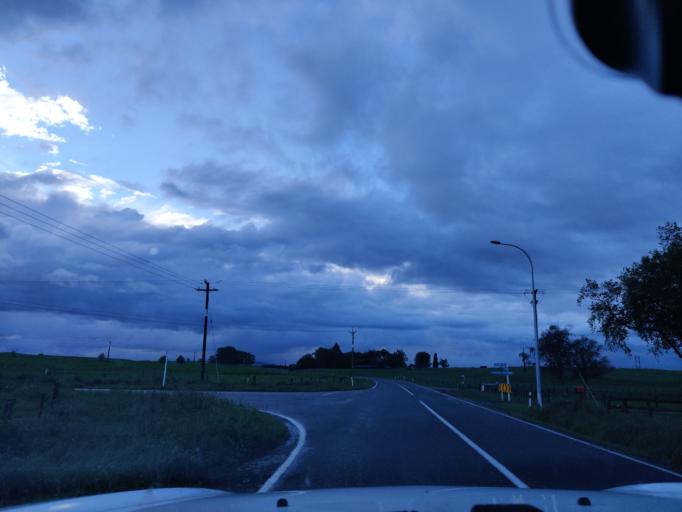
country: NZ
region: Waikato
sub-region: South Waikato District
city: Tokoroa
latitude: -38.2247
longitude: 175.8332
